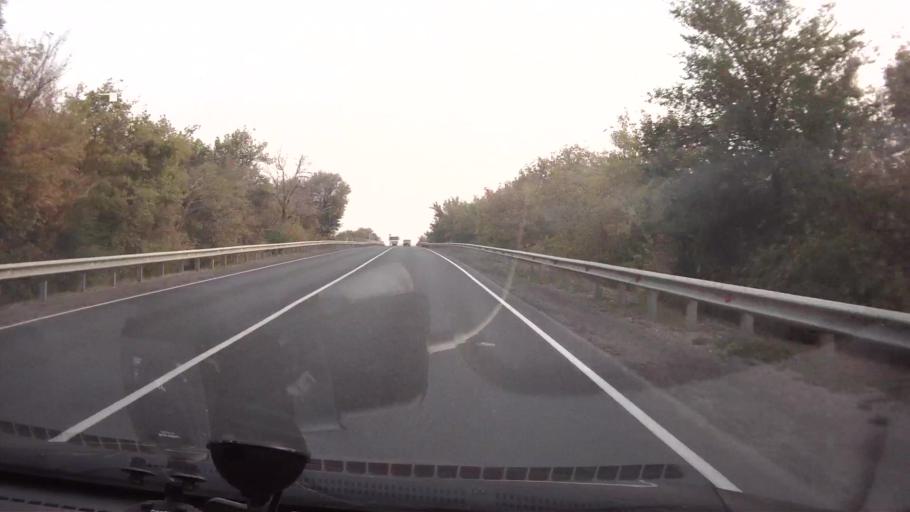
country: RU
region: Saratov
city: Krasnyy Oktyabr'
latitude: 51.4035
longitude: 45.7006
